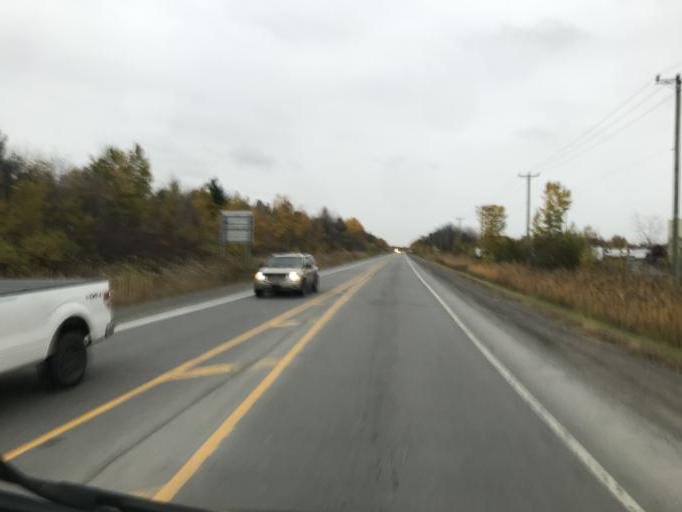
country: CA
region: Quebec
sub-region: Lanaudiere
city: Lorraine
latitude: 45.6888
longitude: -73.7800
